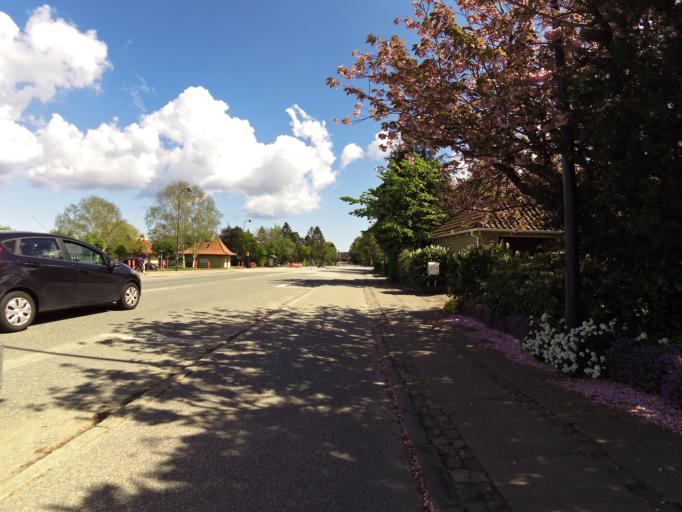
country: DK
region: Capital Region
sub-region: Gentofte Kommune
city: Charlottenlund
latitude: 55.7371
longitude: 12.5483
